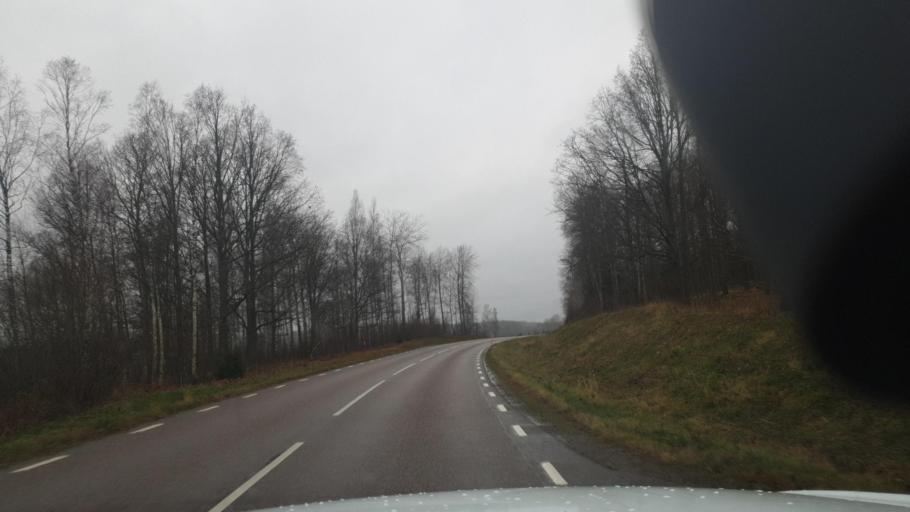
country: SE
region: Vaermland
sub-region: Arvika Kommun
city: Arvika
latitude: 59.5203
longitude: 12.6246
